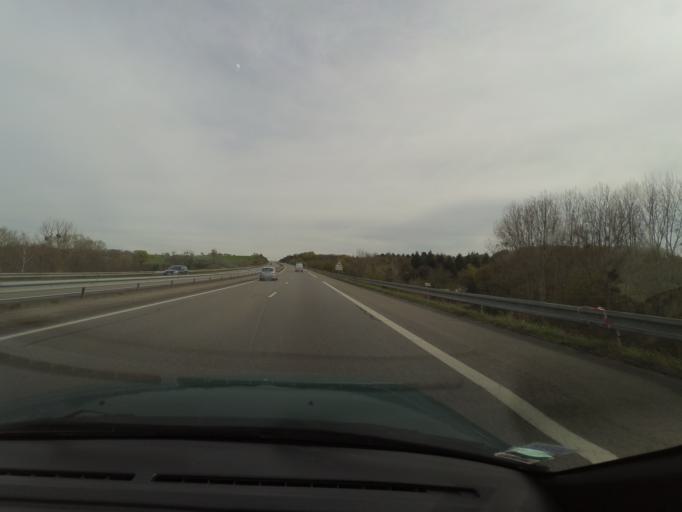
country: FR
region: Pays de la Loire
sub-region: Departement de la Loire-Atlantique
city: Mauves-sur-Loire
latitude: 47.3126
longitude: -1.4127
